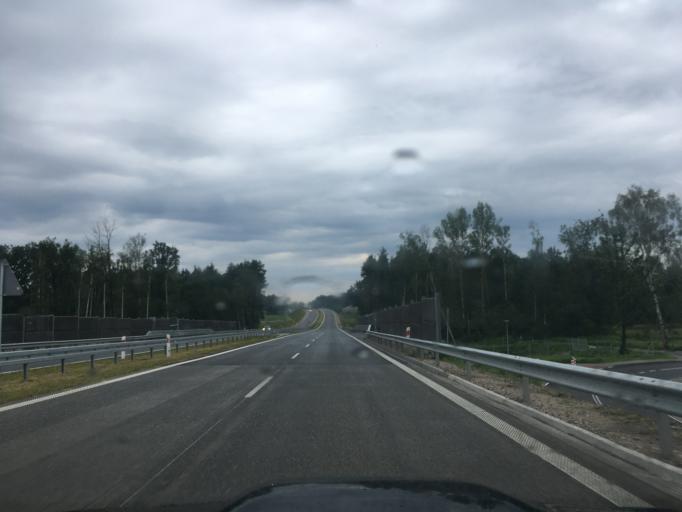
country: PL
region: Masovian Voivodeship
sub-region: Powiat piaseczynski
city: Baniocha
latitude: 51.9882
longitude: 21.1726
